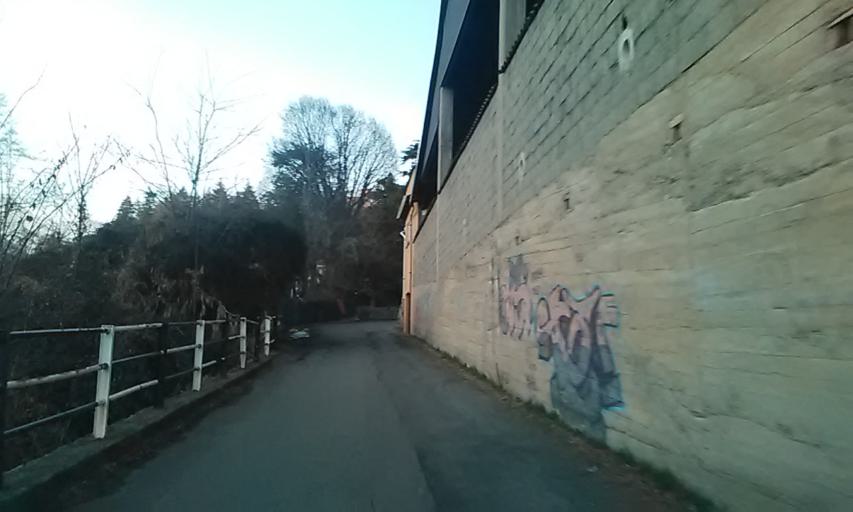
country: IT
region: Piedmont
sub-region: Provincia di Biella
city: Biella
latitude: 45.5703
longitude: 8.0630
